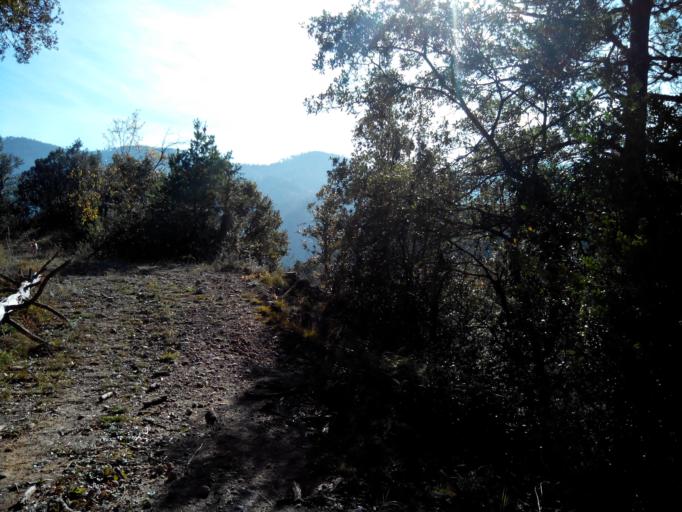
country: ES
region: Catalonia
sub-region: Provincia de Barcelona
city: Vilada
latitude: 42.1075
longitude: 1.9383
